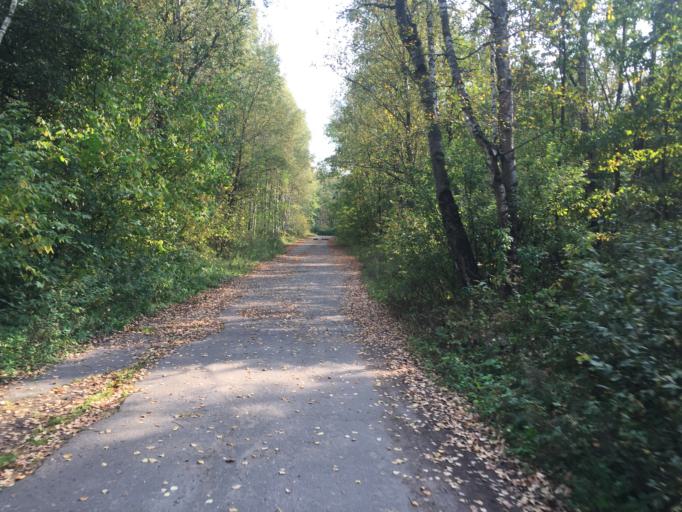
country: RU
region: Moscow
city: Babushkin
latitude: 55.8482
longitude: 37.7195
